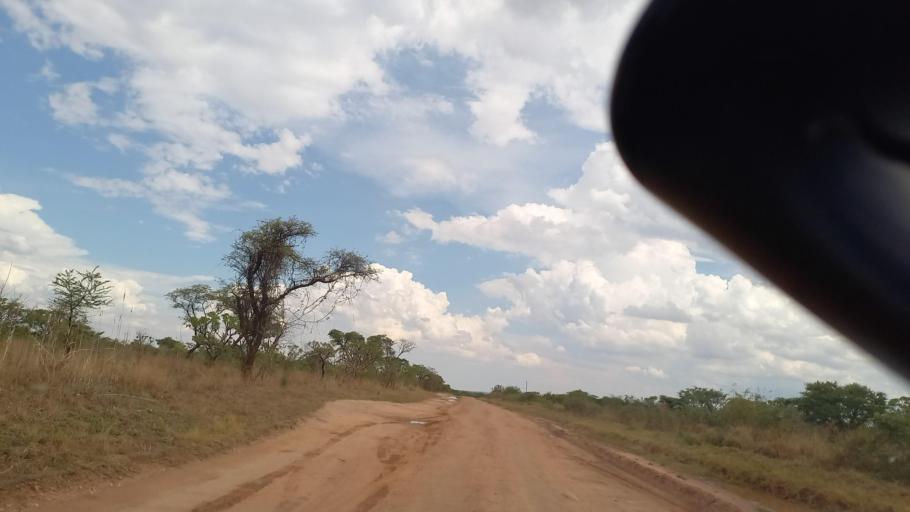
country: ZM
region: Southern
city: Nakambala
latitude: -16.0594
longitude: 27.9908
